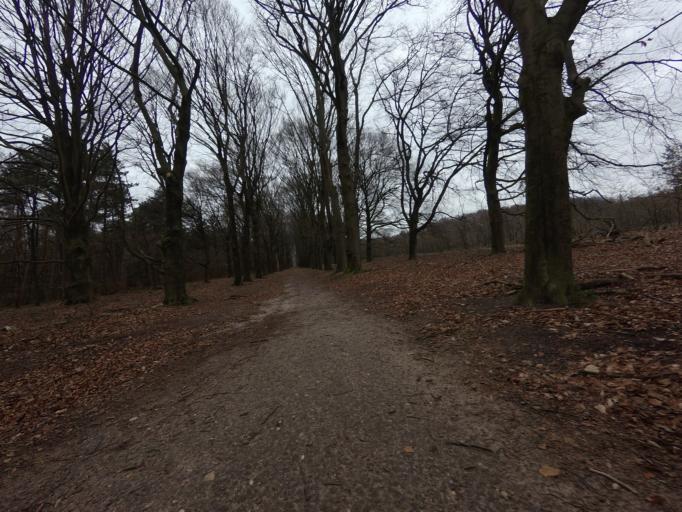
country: NL
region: Utrecht
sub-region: Gemeente Utrechtse Heuvelrug
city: Doorn
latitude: 52.0388
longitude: 5.3642
